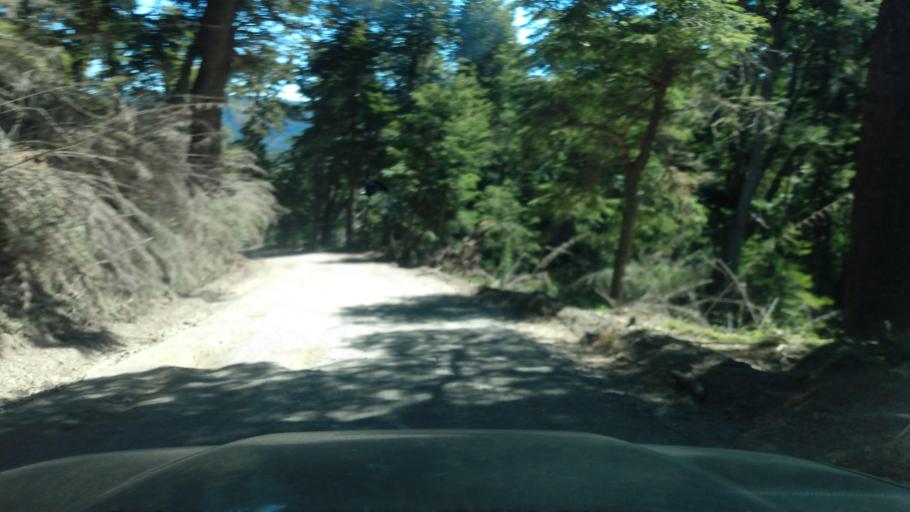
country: AR
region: Neuquen
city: Villa La Angostura
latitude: -40.6050
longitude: -71.6420
